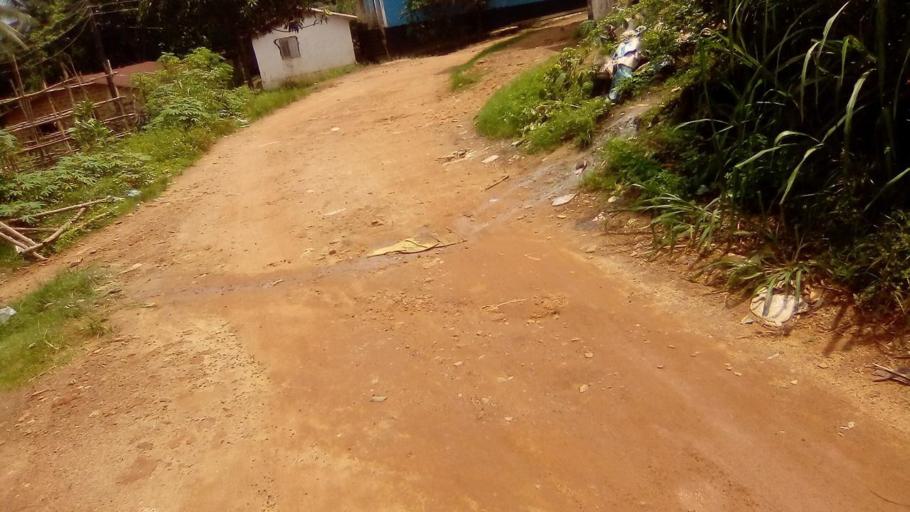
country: SL
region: Southern Province
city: Bo
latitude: 7.9399
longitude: -11.7337
